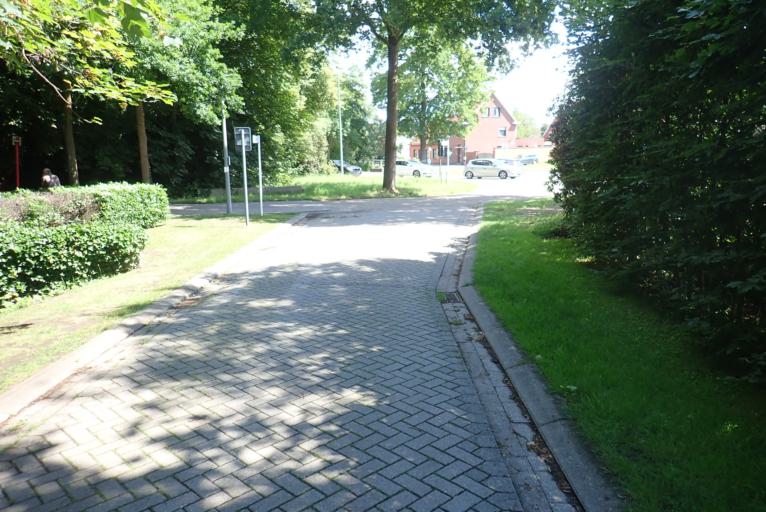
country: BE
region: Flanders
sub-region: Provincie Antwerpen
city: Oostmalle
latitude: 51.3027
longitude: 4.7295
